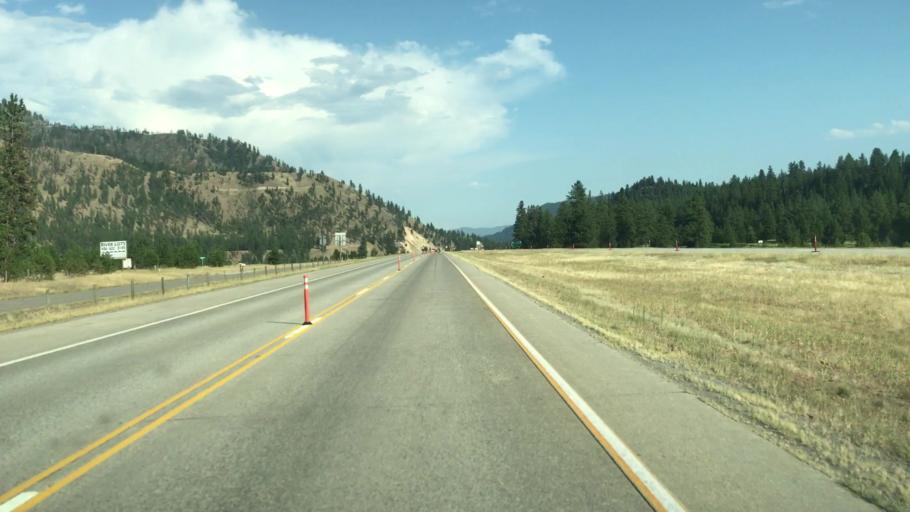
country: US
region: Montana
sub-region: Mineral County
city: Superior
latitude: 47.2311
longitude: -114.9802
